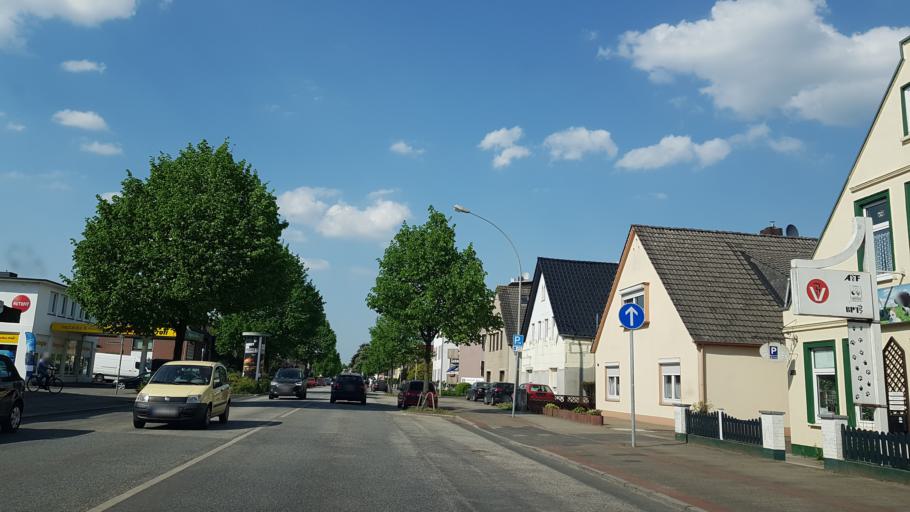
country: DE
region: Lower Saxony
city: Langen
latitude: 53.5908
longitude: 8.5975
